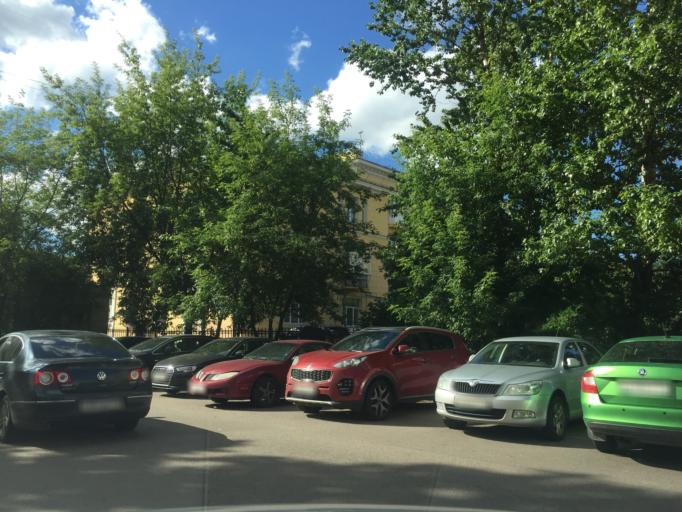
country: RU
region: St.-Petersburg
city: Kupchino
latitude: 59.8285
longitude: 30.3268
